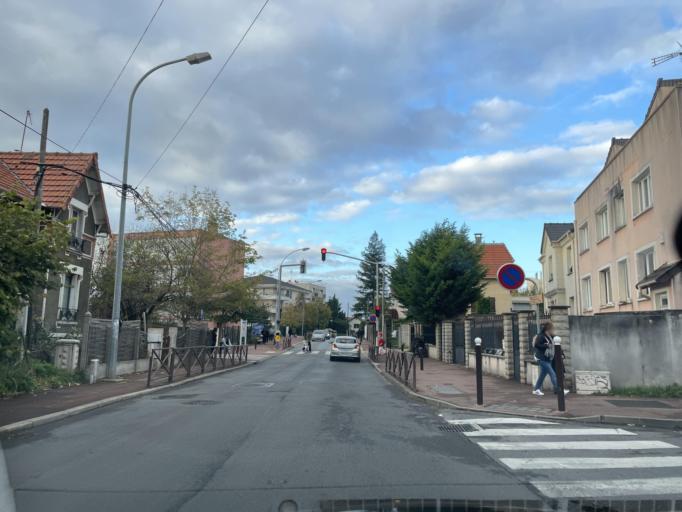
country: FR
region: Ile-de-France
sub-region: Departement du Val-de-Marne
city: Creteil
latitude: 48.7849
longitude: 2.4632
